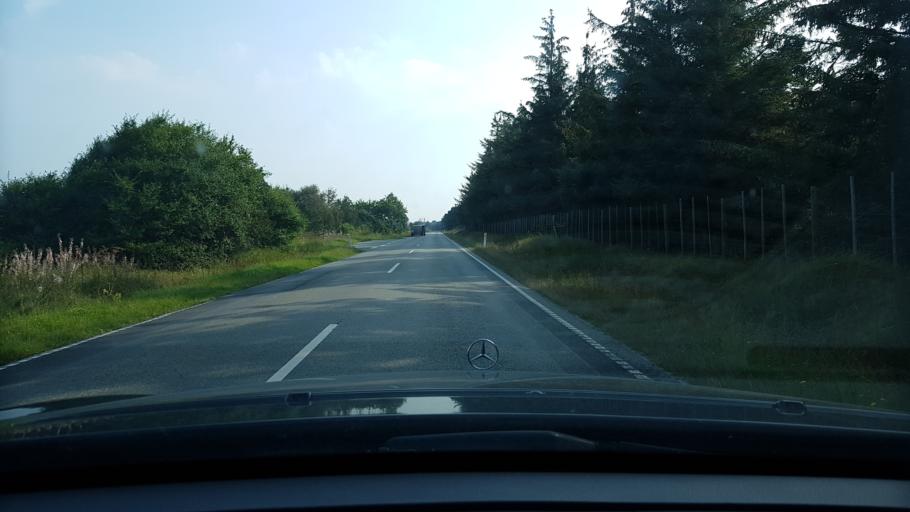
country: DK
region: North Denmark
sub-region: Alborg Kommune
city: Hals
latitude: 56.8307
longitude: 10.2684
